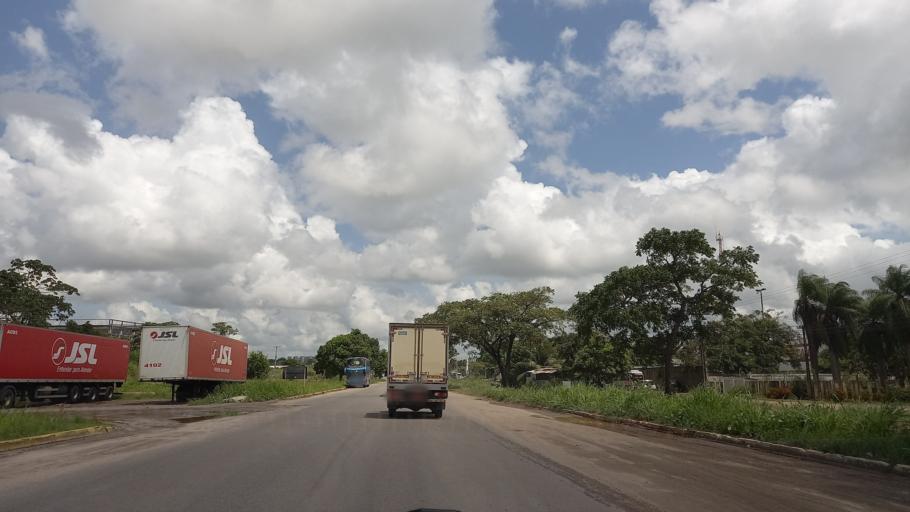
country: BR
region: Pernambuco
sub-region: Cabo De Santo Agostinho
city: Cabo
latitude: -8.2482
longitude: -35.0007
